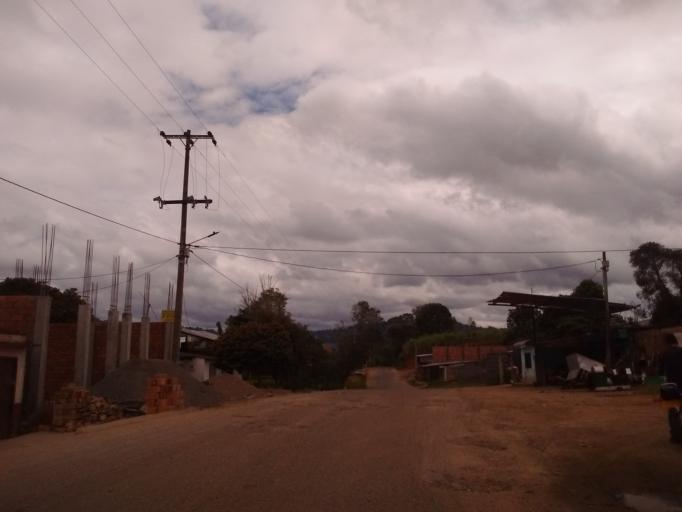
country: CO
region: Huila
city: Isnos
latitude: 1.9371
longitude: -76.2192
